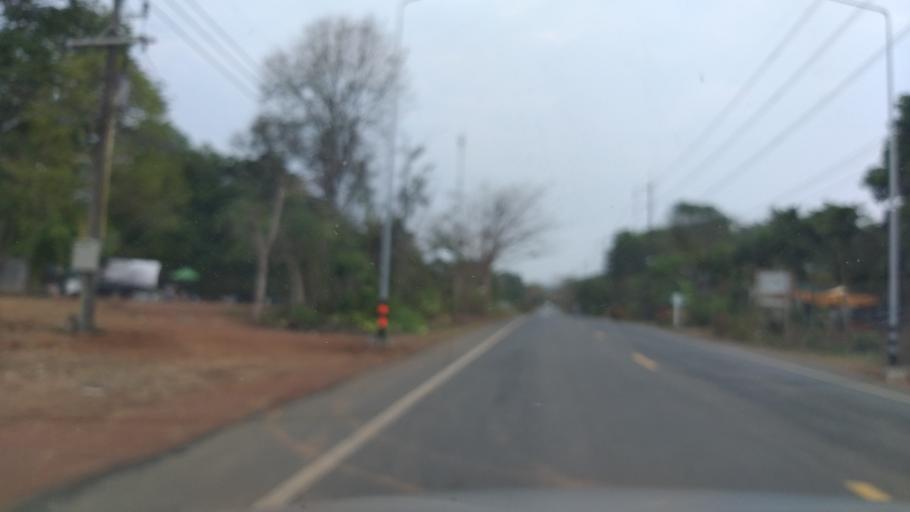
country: TH
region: Trat
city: Khao Saming
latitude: 12.2899
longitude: 102.3222
